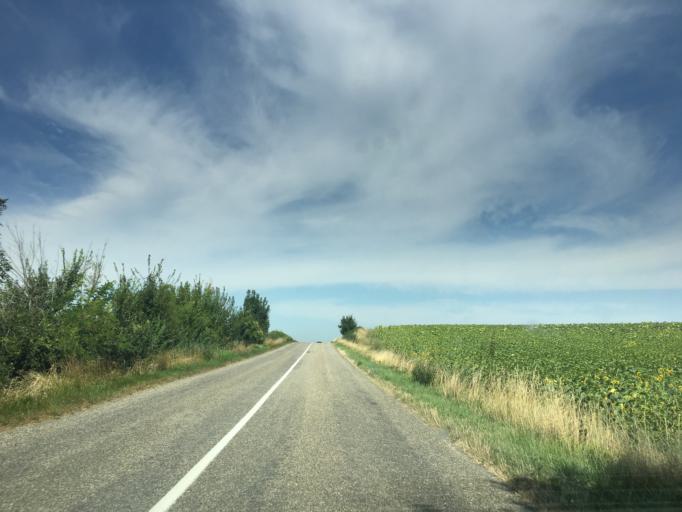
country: FR
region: Midi-Pyrenees
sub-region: Departement du Gers
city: Fleurance
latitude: 43.8742
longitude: 0.7541
